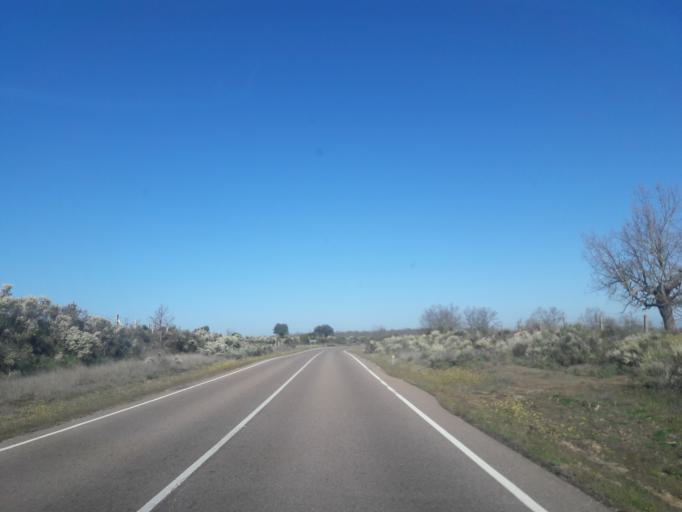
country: ES
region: Castille and Leon
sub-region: Provincia de Salamanca
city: Valderrodrigo
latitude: 41.0759
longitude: -6.5499
